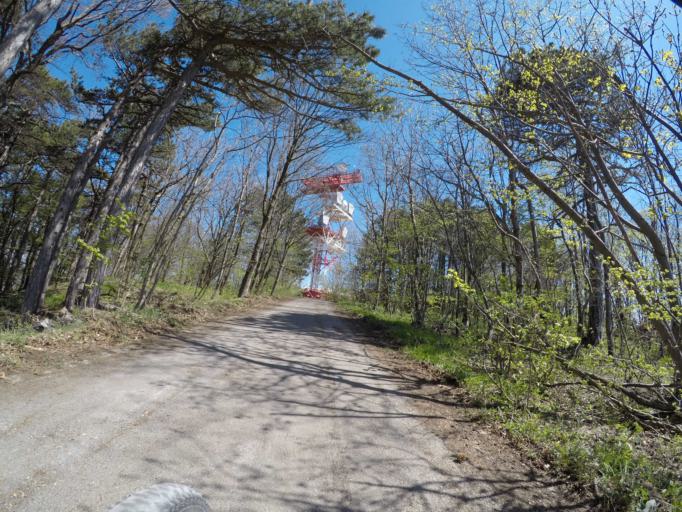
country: AT
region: Lower Austria
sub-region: Politischer Bezirk Modling
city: Gumpoldskirchen
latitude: 48.0525
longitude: 16.2514
